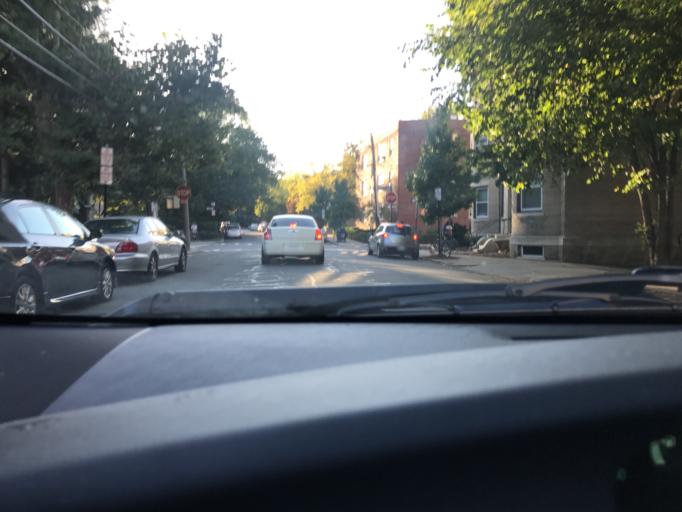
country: US
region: Massachusetts
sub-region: Norfolk County
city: Brookline
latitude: 42.3402
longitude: -71.1233
